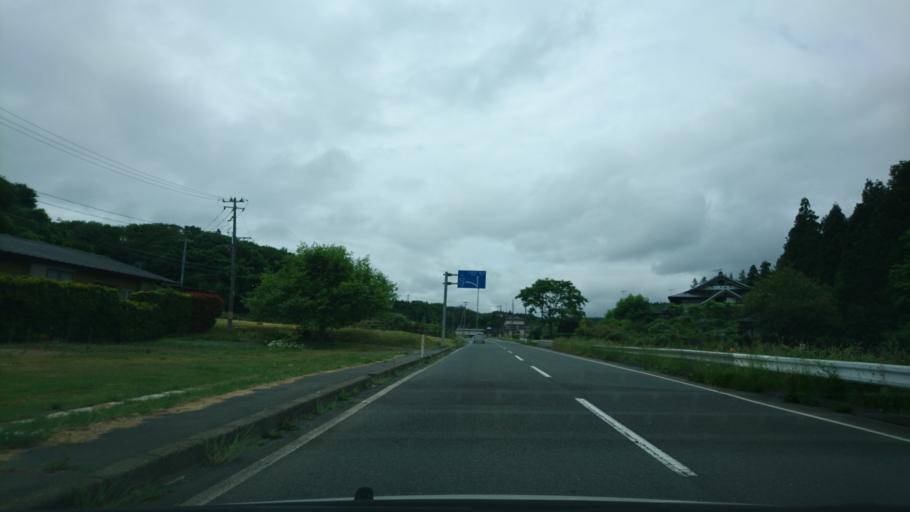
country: JP
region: Iwate
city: Ichinoseki
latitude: 38.8905
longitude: 141.1201
